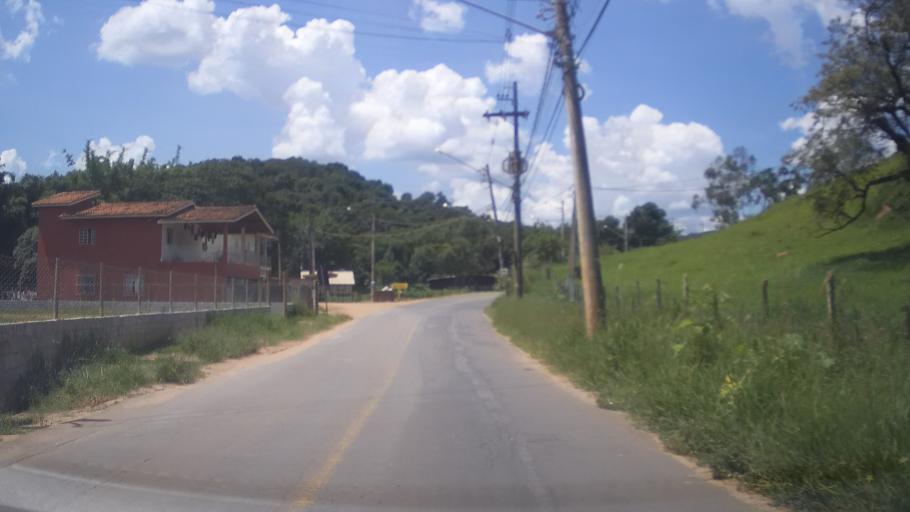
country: BR
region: Sao Paulo
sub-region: Jarinu
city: Jarinu
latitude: -23.1265
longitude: -46.8073
